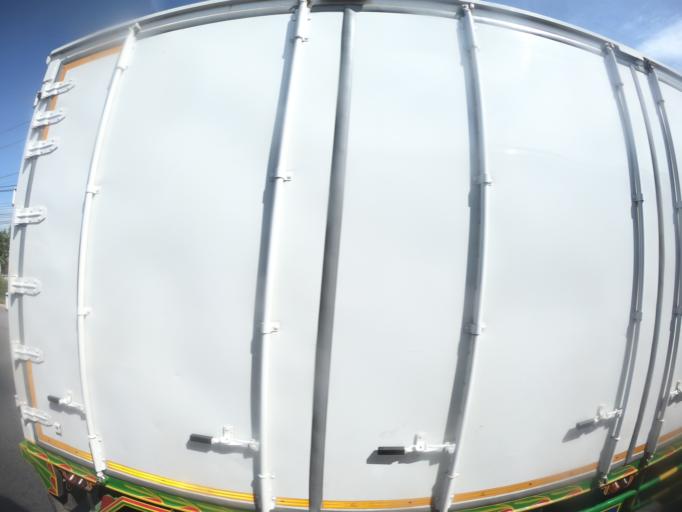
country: TH
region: Khon Kaen
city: Khon Kaen
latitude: 16.4445
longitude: 102.9644
